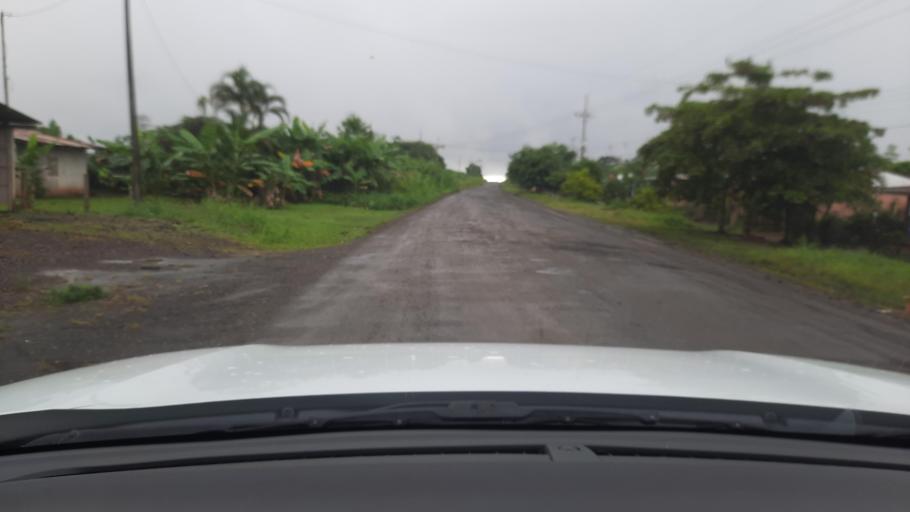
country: CR
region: Alajuela
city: San Jose
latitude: 11.0121
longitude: -85.3421
